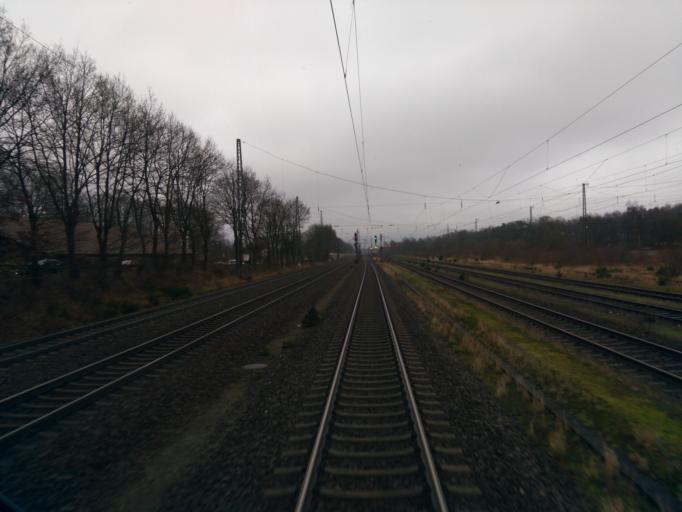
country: DE
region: Lower Saxony
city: Buchholz in der Nordheide
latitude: 53.3210
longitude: 9.8455
